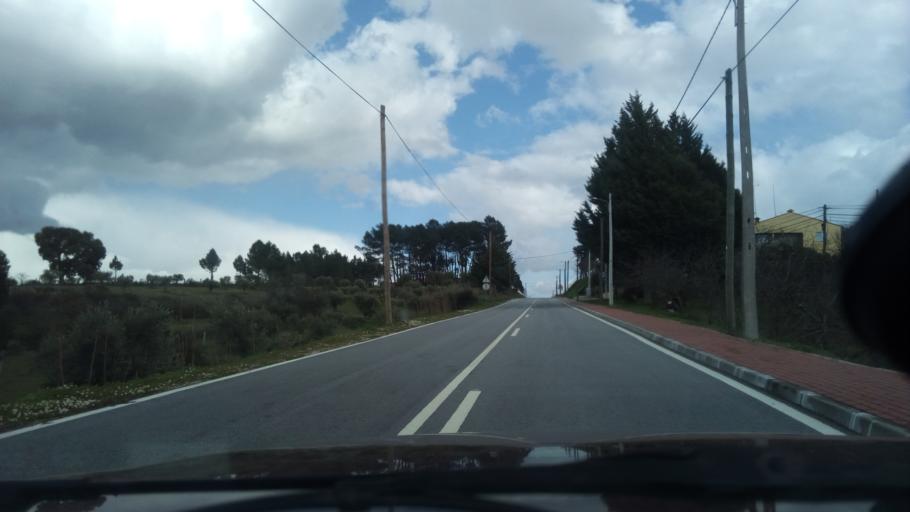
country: PT
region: Guarda
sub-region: Celorico da Beira
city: Celorico da Beira
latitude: 40.6408
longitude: -7.3788
